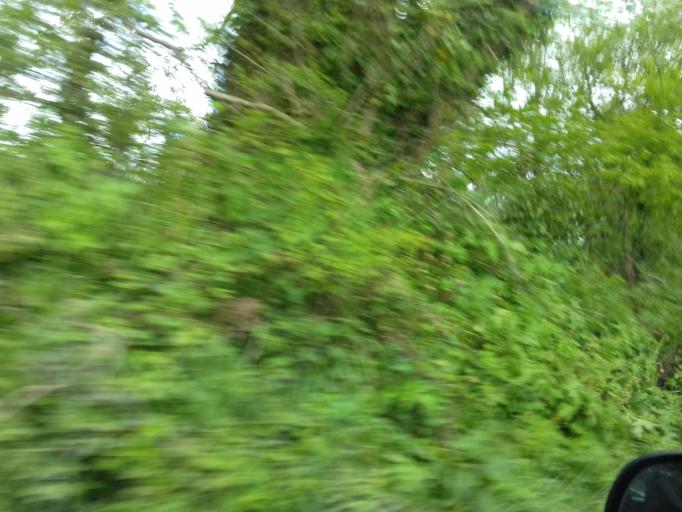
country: IE
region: Leinster
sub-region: Loch Garman
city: Castlebridge
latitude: 52.3817
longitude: -6.5020
